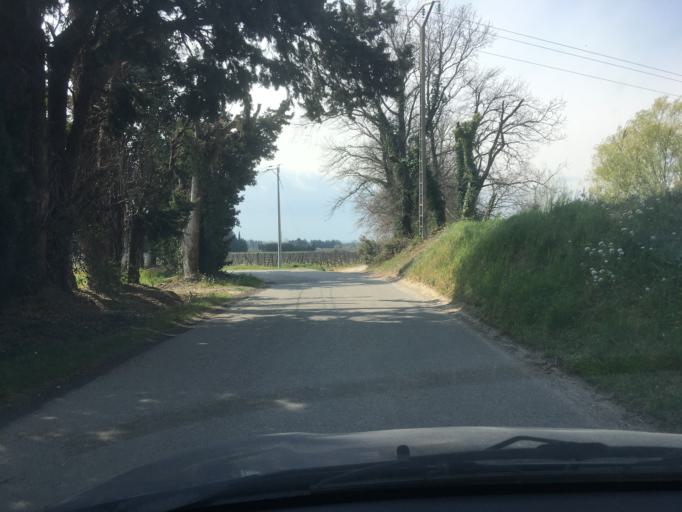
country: FR
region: Provence-Alpes-Cote d'Azur
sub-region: Departement du Vaucluse
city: Aubignan
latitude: 44.0954
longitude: 5.0187
